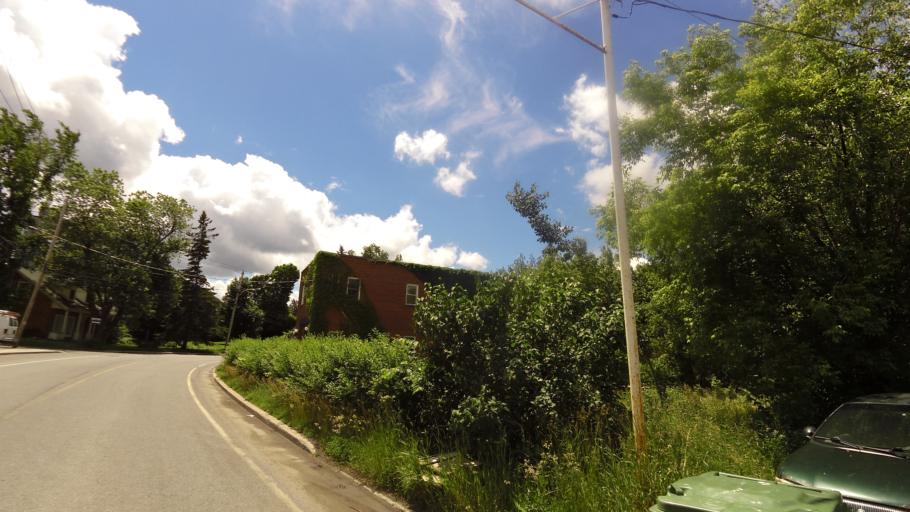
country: CA
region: Quebec
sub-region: Laurentides
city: Lachute
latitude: 45.5618
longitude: -74.3353
